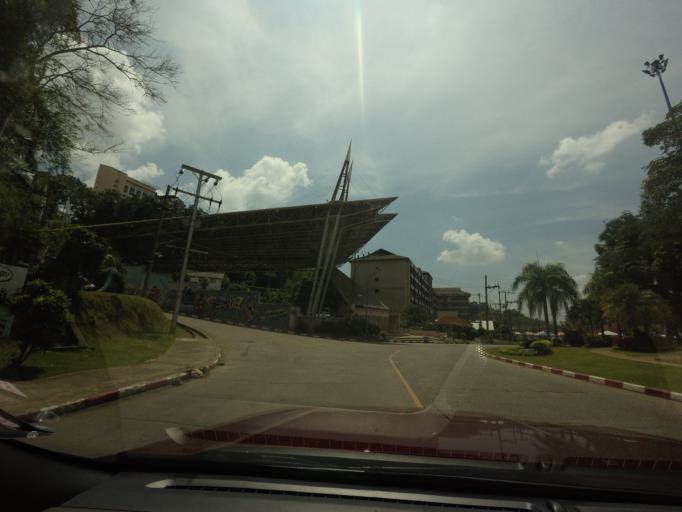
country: TH
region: Yala
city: Betong
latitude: 5.7684
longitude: 101.0729
